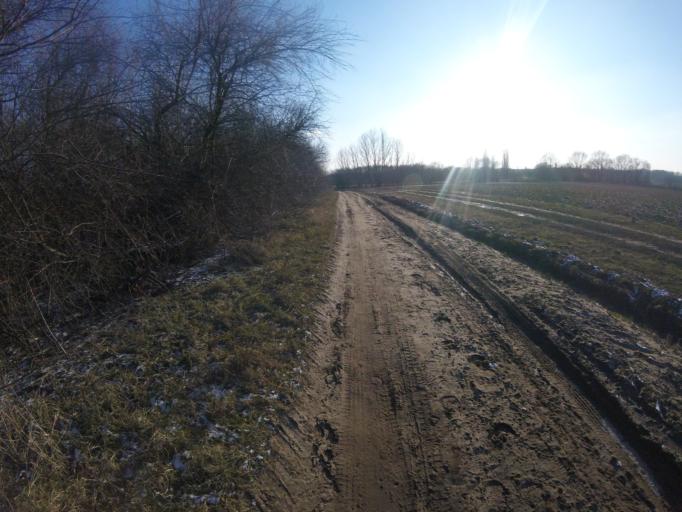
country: HU
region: Pest
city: Ecser
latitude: 47.4496
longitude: 19.2909
